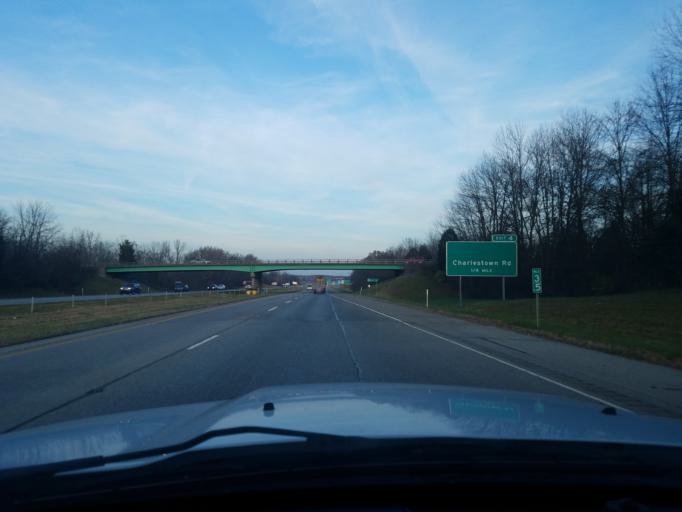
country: US
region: Indiana
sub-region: Floyd County
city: New Albany
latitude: 38.3386
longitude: -85.8126
